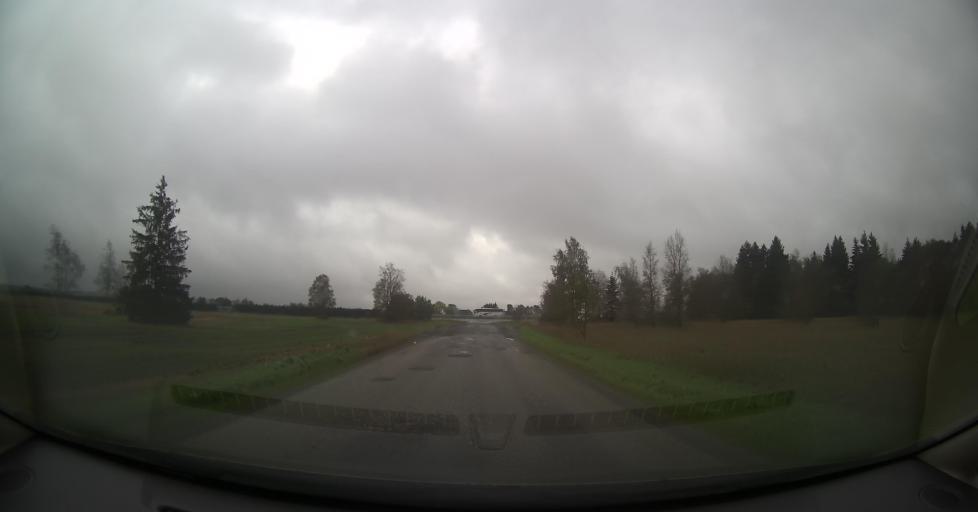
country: EE
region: Harju
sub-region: Raasiku vald
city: Arukula
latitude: 59.4447
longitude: 25.1207
